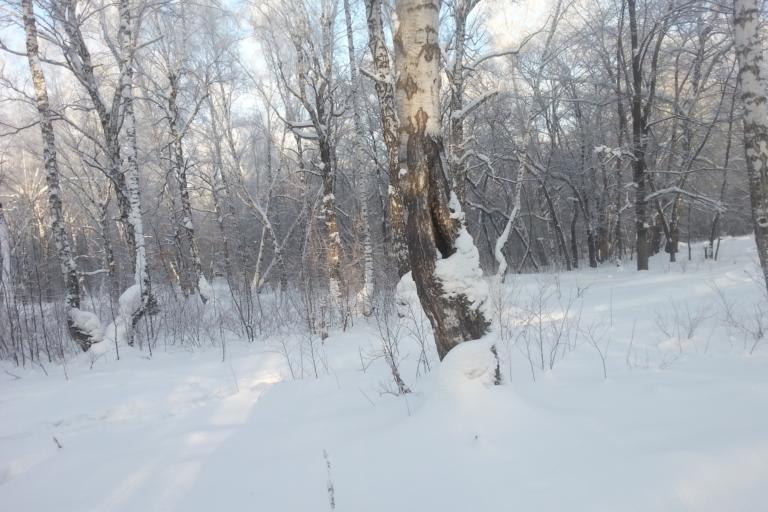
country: RU
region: Altai Krai
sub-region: Gorod Barnaulskiy
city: Barnaul
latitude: 53.3689
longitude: 83.7184
